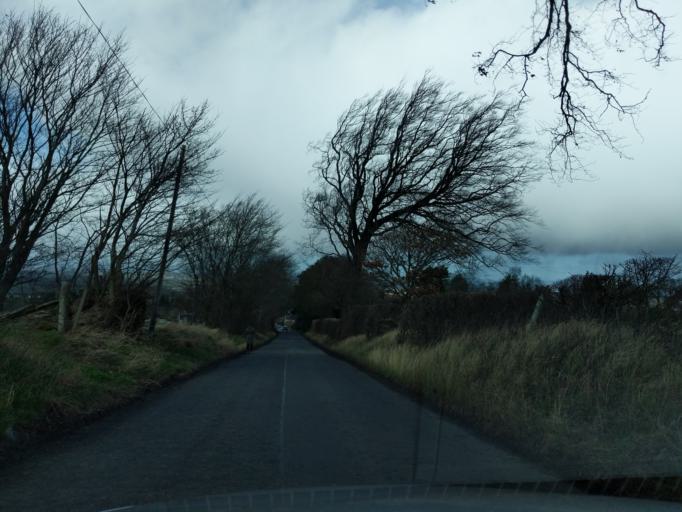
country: GB
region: Scotland
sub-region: Edinburgh
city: Currie
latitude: 55.8901
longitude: -3.3038
